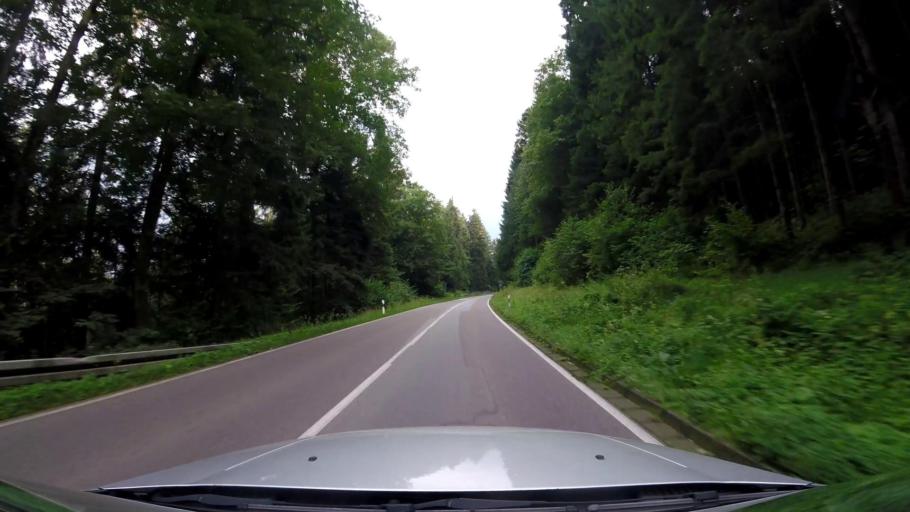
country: DE
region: Baden-Wuerttemberg
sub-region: Regierungsbezirk Stuttgart
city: Durlangen
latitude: 48.8454
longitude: 9.7810
